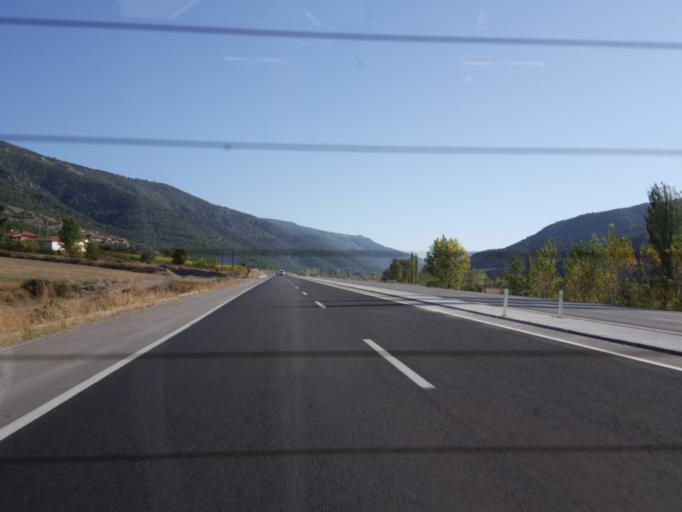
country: TR
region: Tokat
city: Turhal
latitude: 40.4639
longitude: 36.1167
